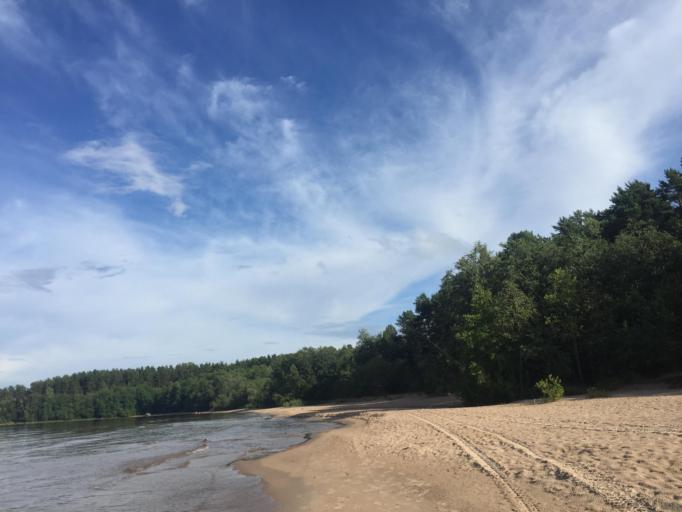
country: RU
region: Leningrad
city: Priozersk
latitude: 60.9752
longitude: 30.2946
